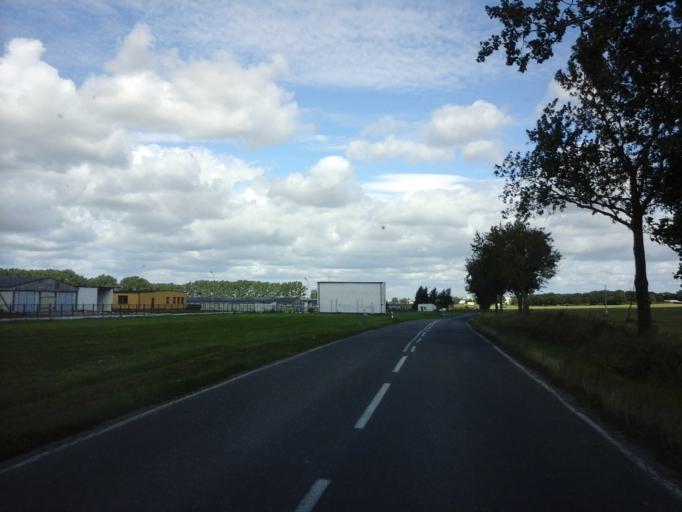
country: PL
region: West Pomeranian Voivodeship
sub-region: Powiat stargardzki
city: Stargard Szczecinski
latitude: 53.2730
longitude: 15.0852
